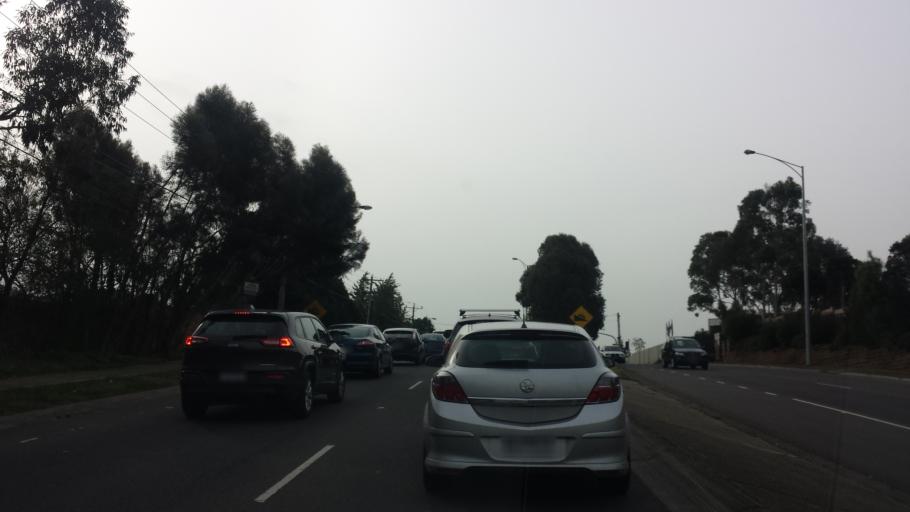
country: AU
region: Victoria
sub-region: Manningham
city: Templestowe Lower
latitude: -37.7640
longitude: 145.1332
